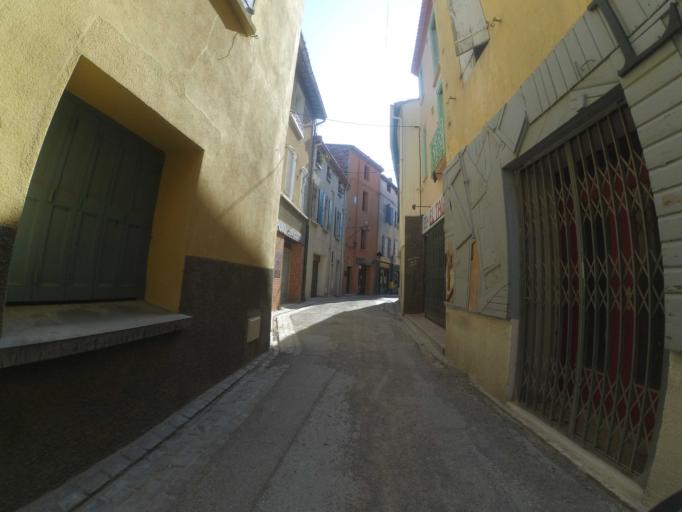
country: FR
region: Languedoc-Roussillon
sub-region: Departement des Pyrenees-Orientales
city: Thuir
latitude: 42.6339
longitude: 2.7553
